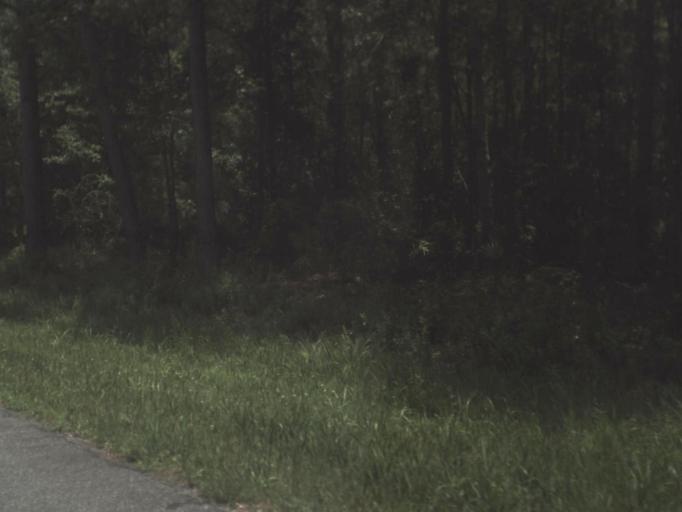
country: US
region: Florida
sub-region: Lafayette County
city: Mayo
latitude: 29.9149
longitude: -83.2890
